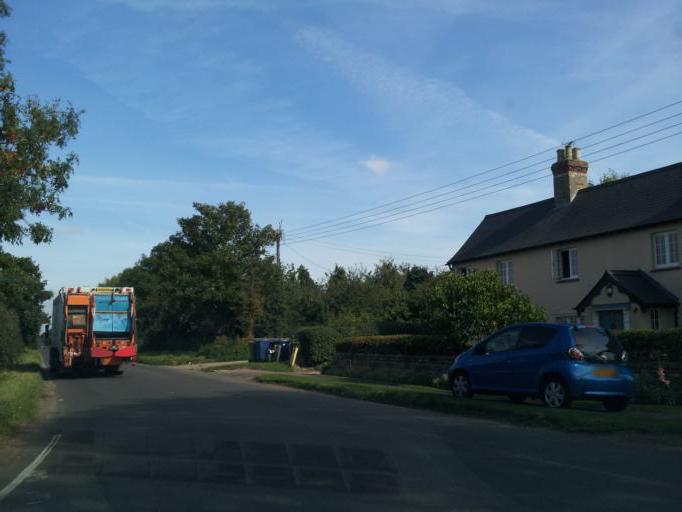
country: GB
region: England
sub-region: Cambridgeshire
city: Waterbeach
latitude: 52.2709
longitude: 0.1630
